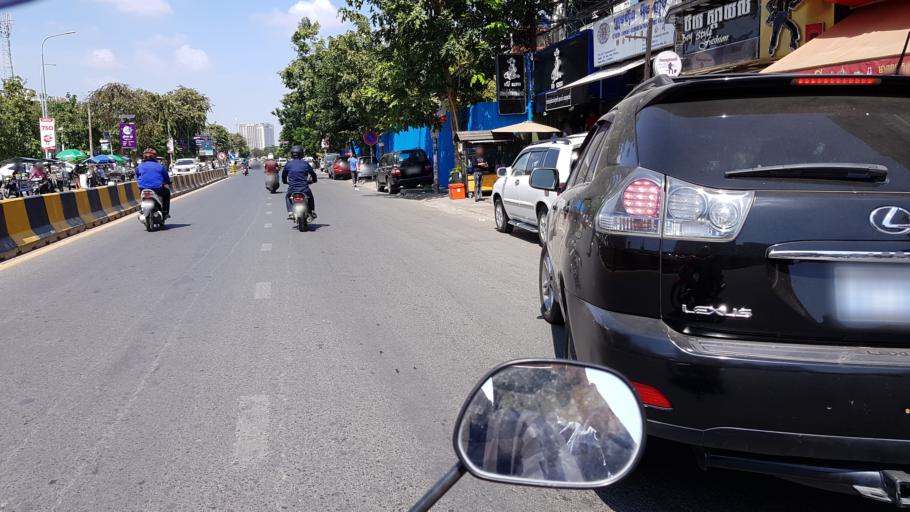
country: KH
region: Phnom Penh
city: Phnom Penh
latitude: 11.5666
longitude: 104.9116
